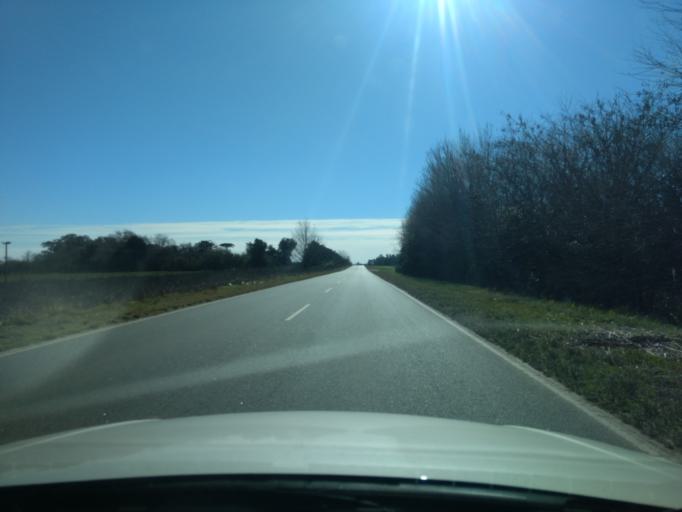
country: AR
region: Buenos Aires
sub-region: Partido de Lujan
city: Lujan
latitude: -34.6165
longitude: -59.1067
